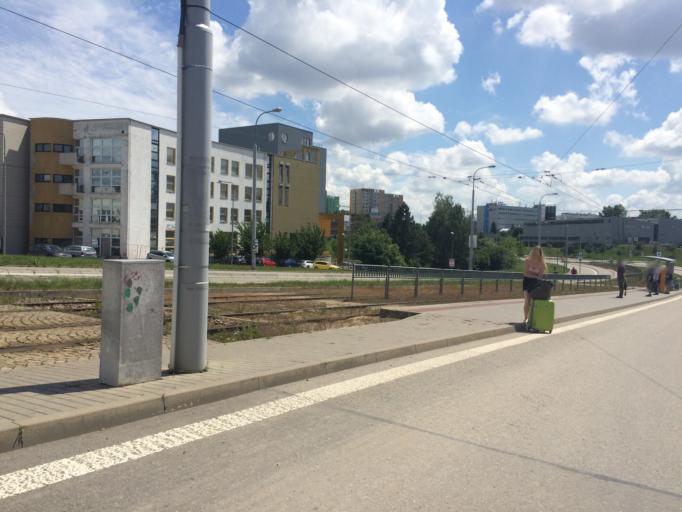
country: CZ
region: South Moravian
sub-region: Mesto Brno
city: Mokra Hora
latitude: 49.2319
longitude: 16.5765
